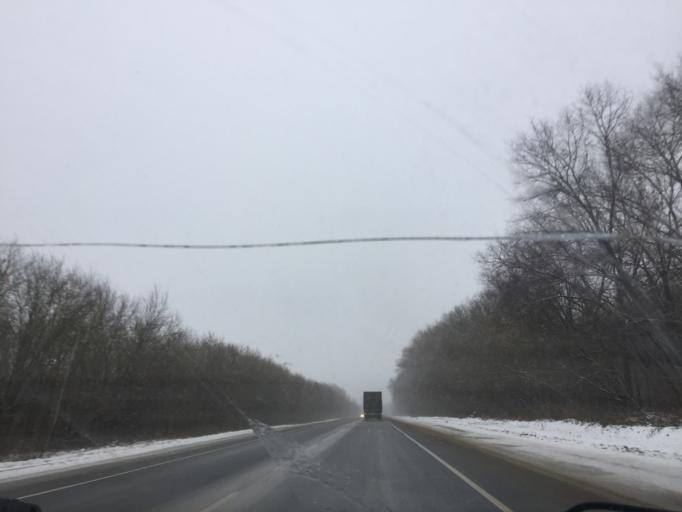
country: RU
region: Tula
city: Plavsk
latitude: 53.7581
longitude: 37.3353
